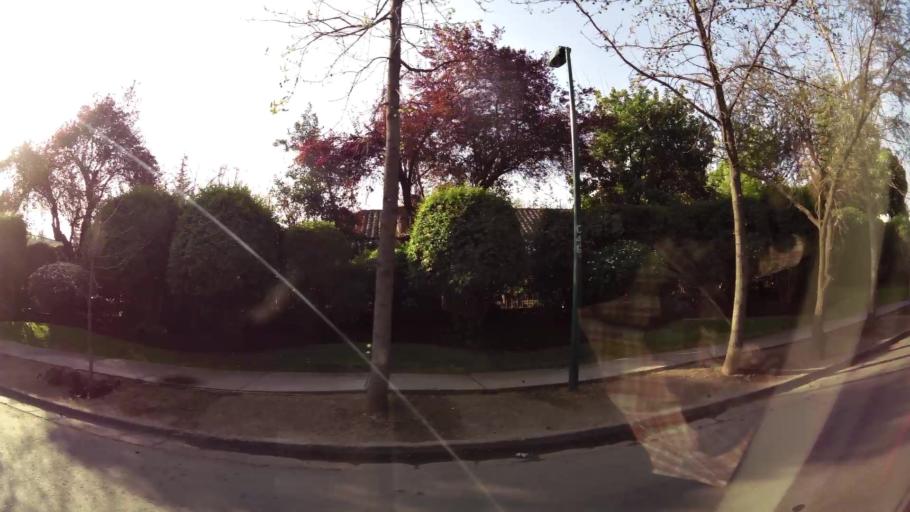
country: CL
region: Santiago Metropolitan
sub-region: Provincia de Santiago
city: Villa Presidente Frei, Nunoa, Santiago, Chile
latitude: -33.3595
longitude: -70.5319
